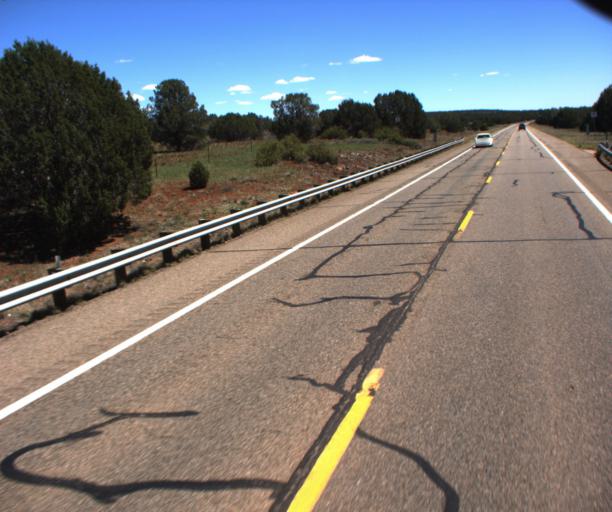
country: US
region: Arizona
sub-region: Yavapai County
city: Paulden
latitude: 35.1291
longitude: -112.4378
